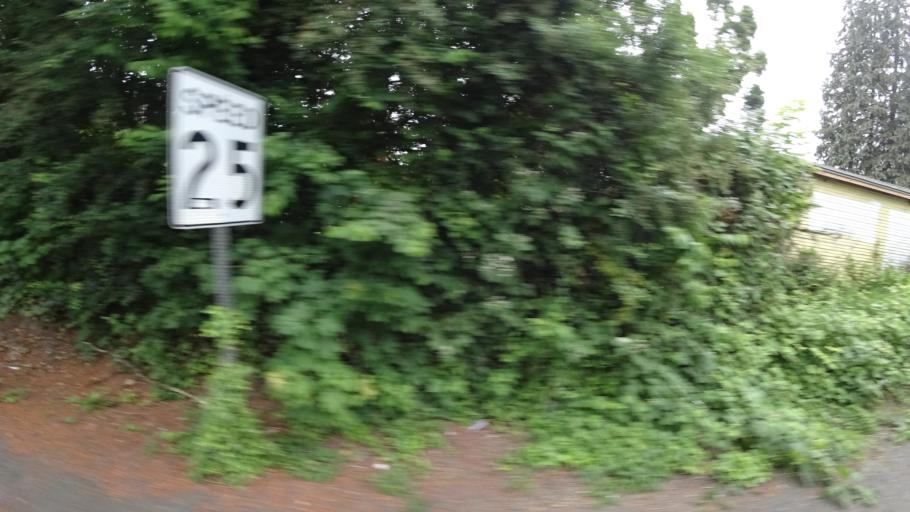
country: US
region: Oregon
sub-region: Washington County
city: Aloha
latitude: 45.5004
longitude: -122.8748
